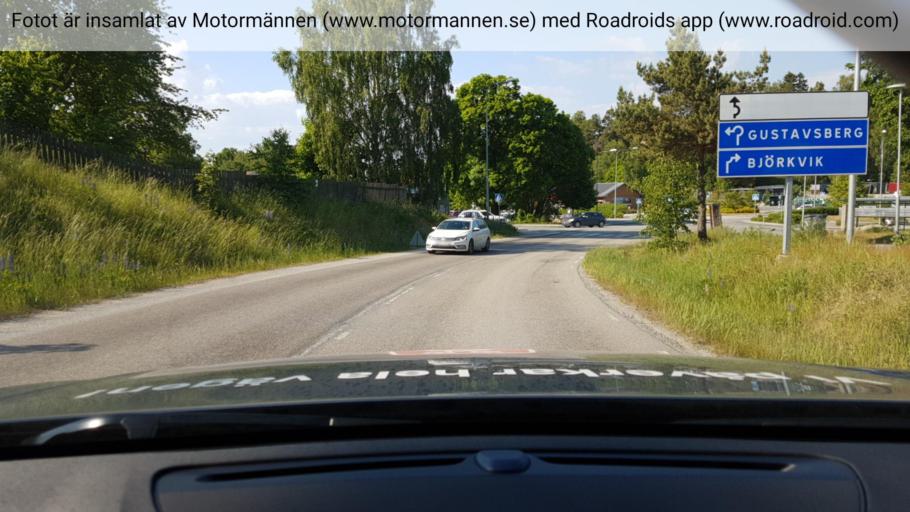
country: SE
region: Stockholm
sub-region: Varmdo Kommun
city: Mortnas
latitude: 59.2810
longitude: 18.4261
